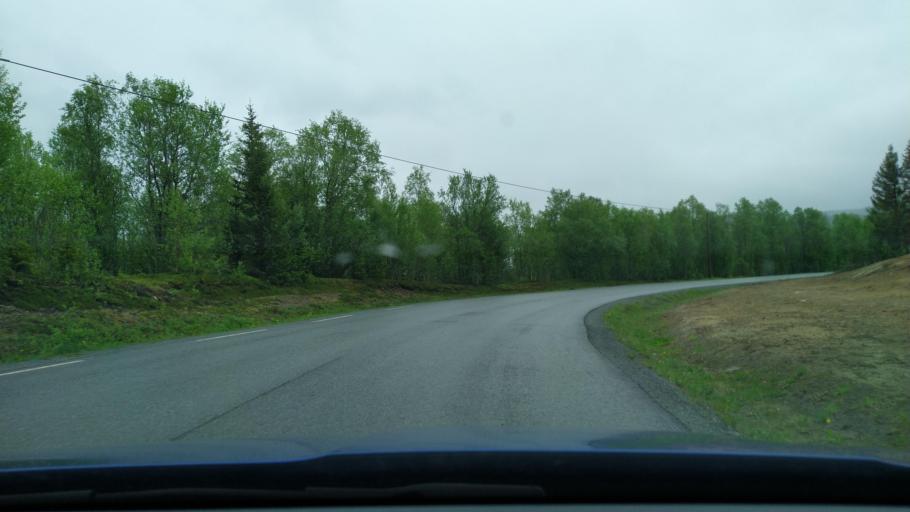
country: NO
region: Troms
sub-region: Dyroy
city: Brostadbotn
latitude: 69.0809
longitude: 17.6991
